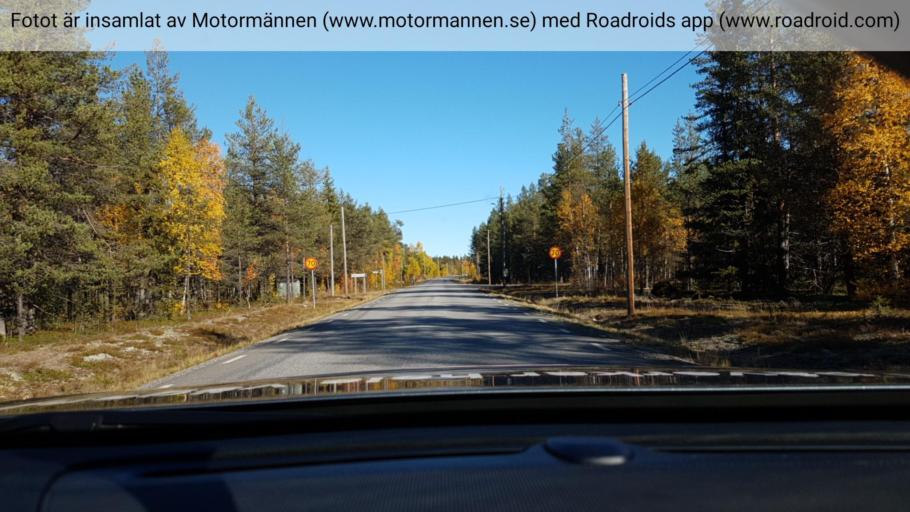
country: SE
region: Norrbotten
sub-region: Gallivare Kommun
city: Gaellivare
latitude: 66.7571
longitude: 21.0134
